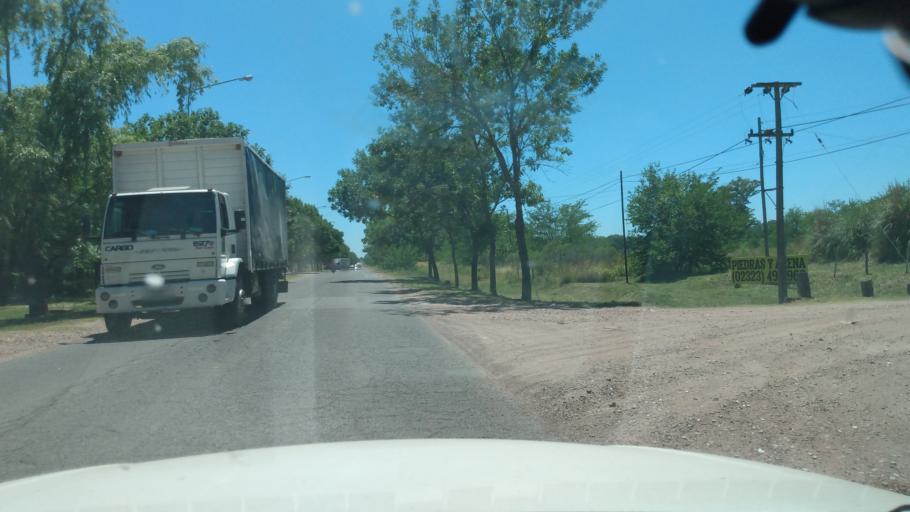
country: AR
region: Buenos Aires
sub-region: Partido de Lujan
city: Lujan
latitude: -34.5798
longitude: -59.1715
